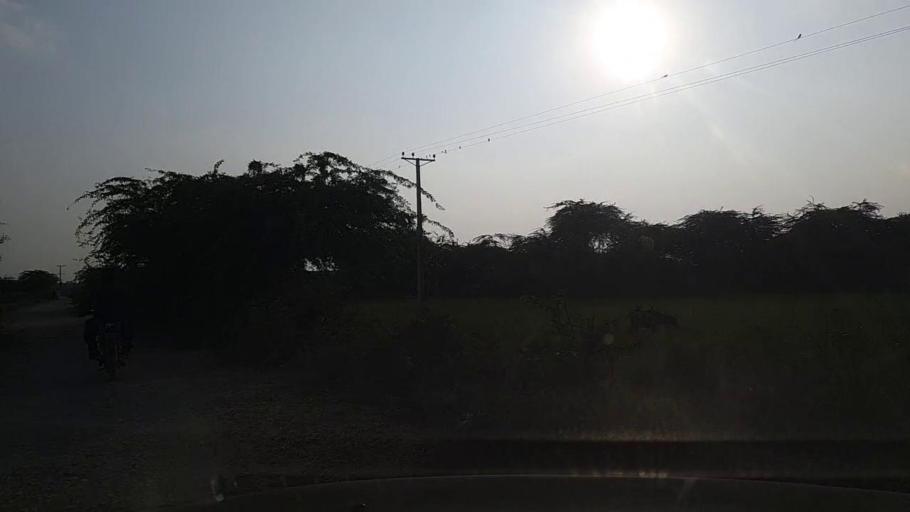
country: PK
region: Sindh
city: Jati
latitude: 24.5385
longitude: 68.3411
